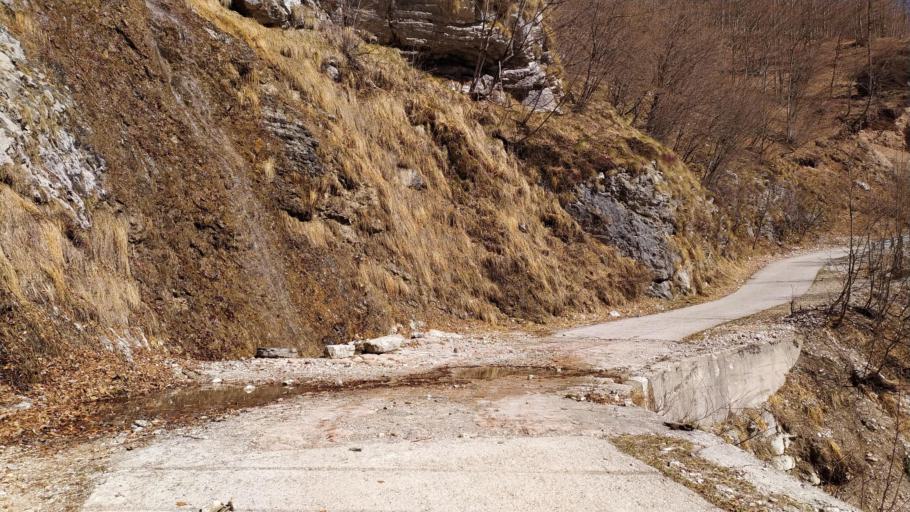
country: IT
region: Friuli Venezia Giulia
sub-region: Provincia di Pordenone
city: Erto
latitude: 46.2905
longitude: 12.3669
